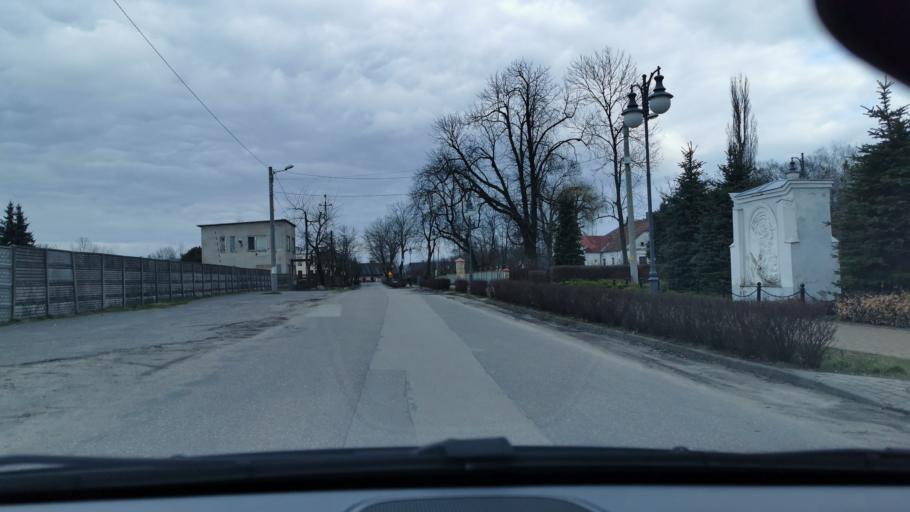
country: PL
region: Masovian Voivodeship
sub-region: Powiat zyrardowski
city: Guzow
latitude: 52.1165
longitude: 20.3336
